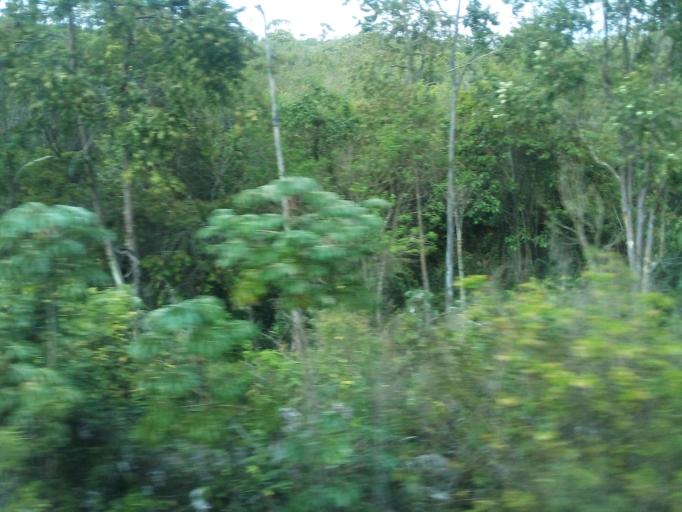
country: BR
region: Minas Gerais
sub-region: Caete
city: Caete
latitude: -19.8933
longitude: -43.7431
